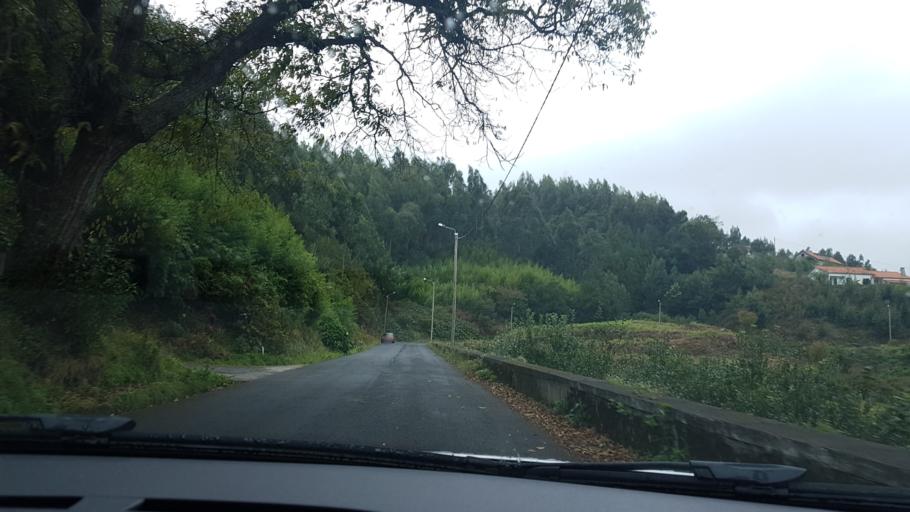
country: PT
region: Madeira
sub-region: Santa Cruz
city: Santa Cruz
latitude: 32.7308
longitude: -16.8094
